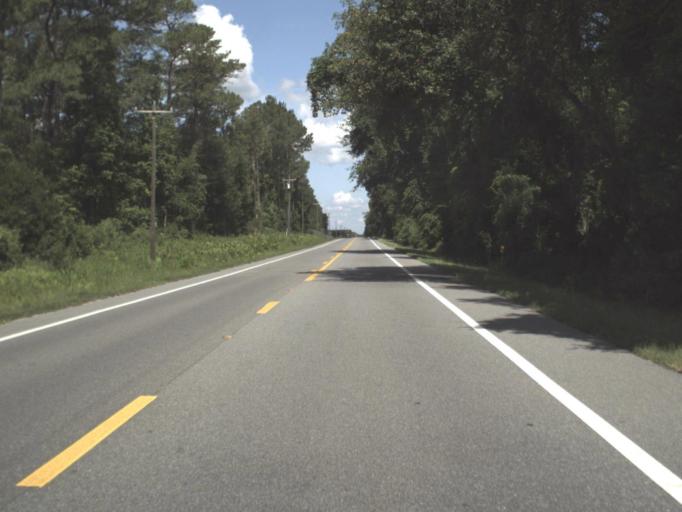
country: US
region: Florida
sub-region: Putnam County
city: Interlachen
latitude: 29.7248
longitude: -81.8373
